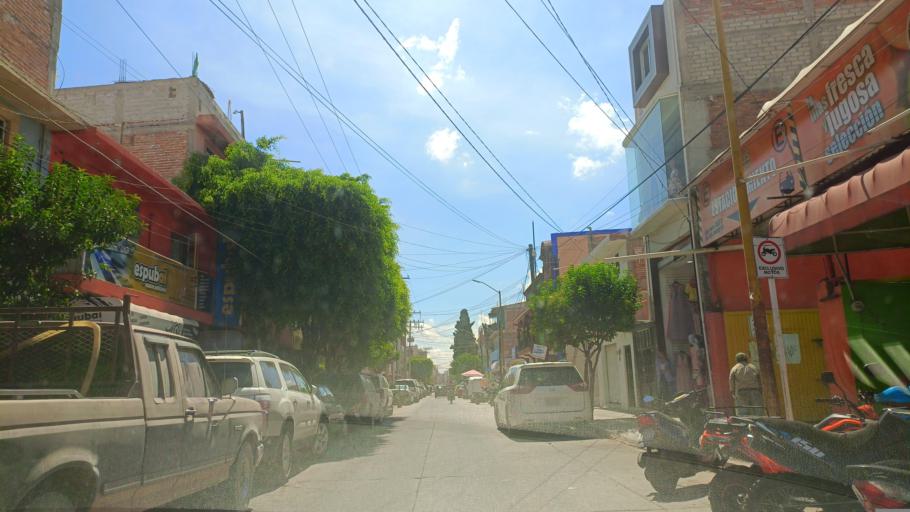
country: MX
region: Guerrero
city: San Luis de la Paz
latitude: 21.2967
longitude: -100.5231
